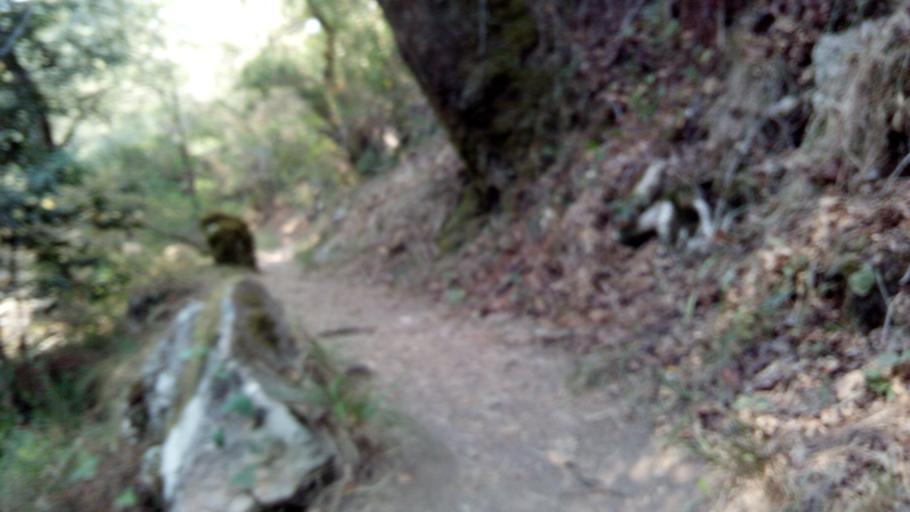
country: ES
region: Galicia
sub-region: Provincia de Pontevedra
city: Oia
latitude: 41.9958
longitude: -8.8133
